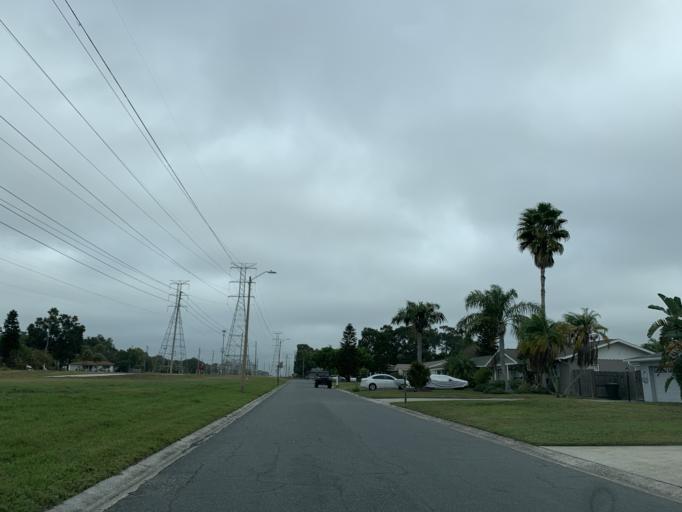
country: US
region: Florida
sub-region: Pinellas County
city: South Highpoint
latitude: 27.9510
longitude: -82.7335
